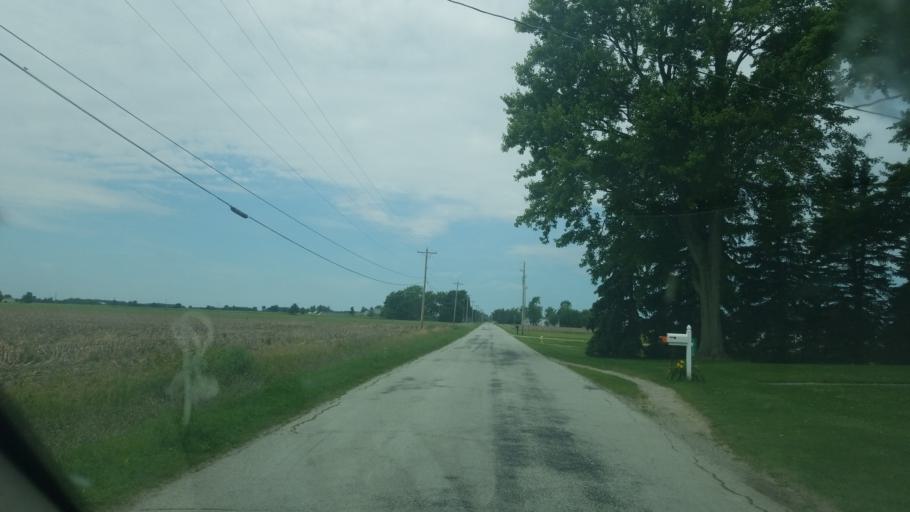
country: US
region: Ohio
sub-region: Wood County
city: North Baltimore
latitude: 41.2685
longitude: -83.6533
